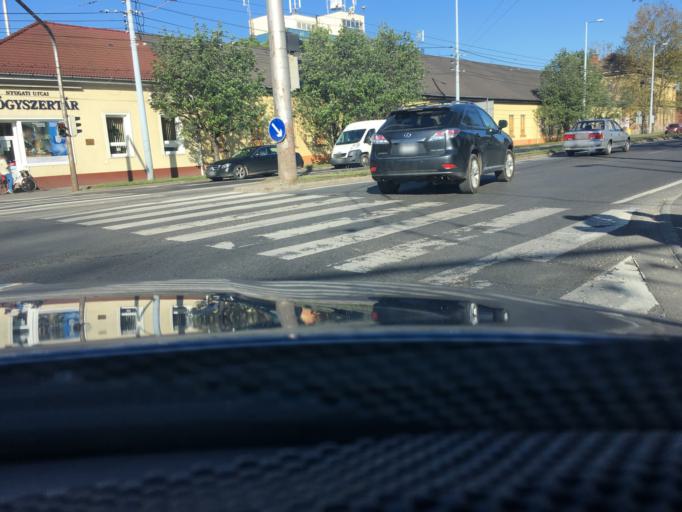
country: HU
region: Hajdu-Bihar
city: Debrecen
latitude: 47.5261
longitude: 21.6172
